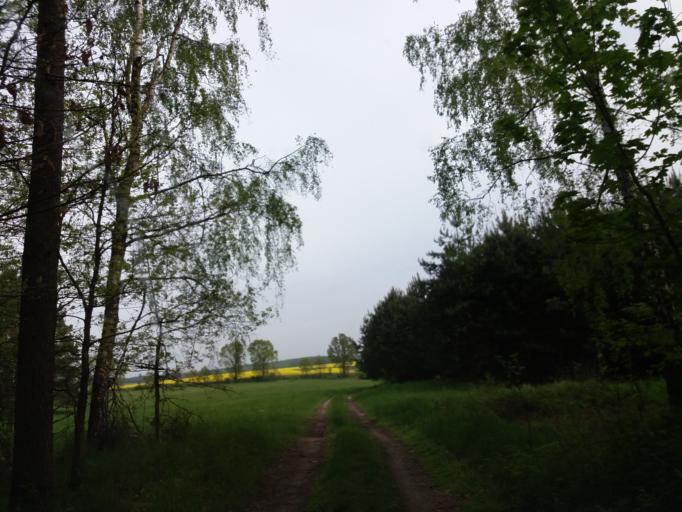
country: PL
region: West Pomeranian Voivodeship
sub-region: Powiat choszczenski
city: Bierzwnik
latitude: 52.9892
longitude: 15.6215
